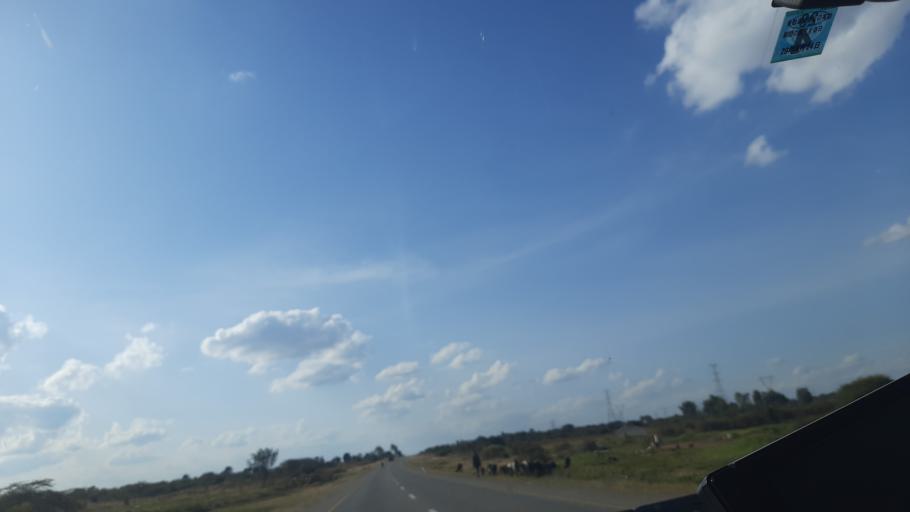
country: TZ
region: Singida
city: Puma
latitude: -5.0379
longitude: 34.7595
